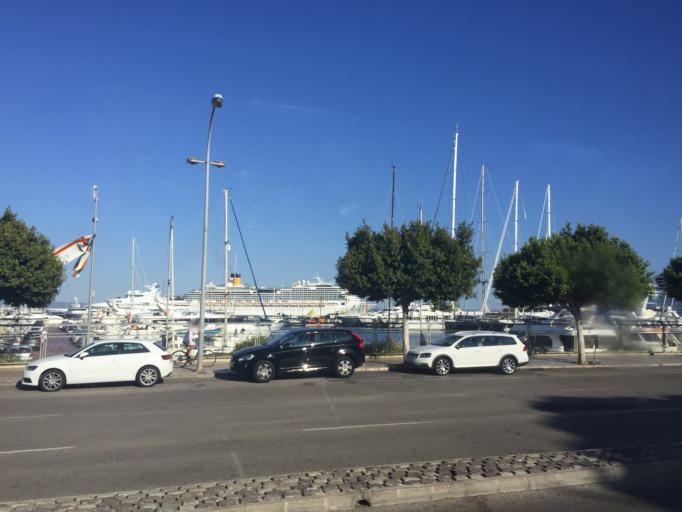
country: ES
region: Balearic Islands
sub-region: Illes Balears
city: Palma
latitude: 39.5585
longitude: 2.6264
